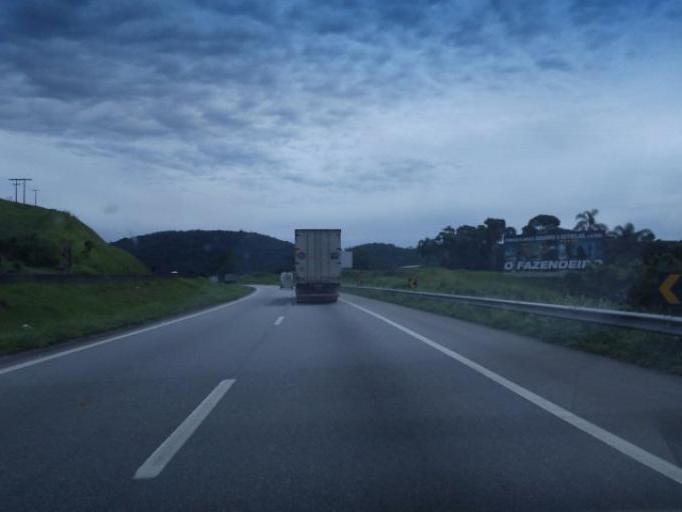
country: BR
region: Sao Paulo
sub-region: Miracatu
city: Miracatu
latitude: -24.1999
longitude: -47.3701
